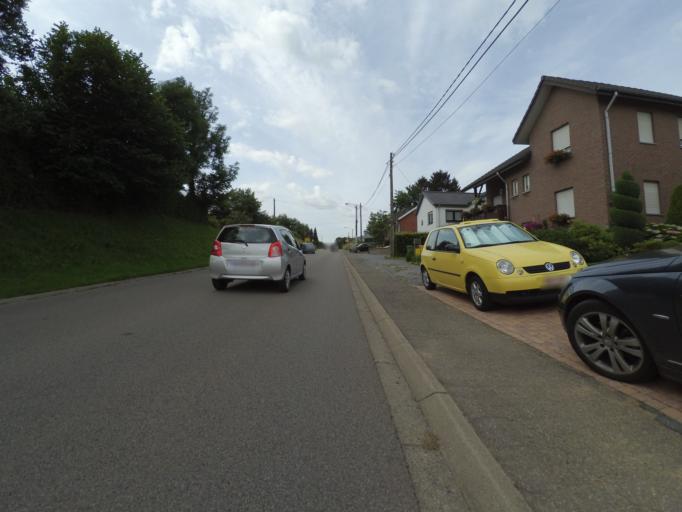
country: BE
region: Wallonia
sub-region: Province de Liege
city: Lontzen
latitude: 50.6721
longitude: 6.0447
